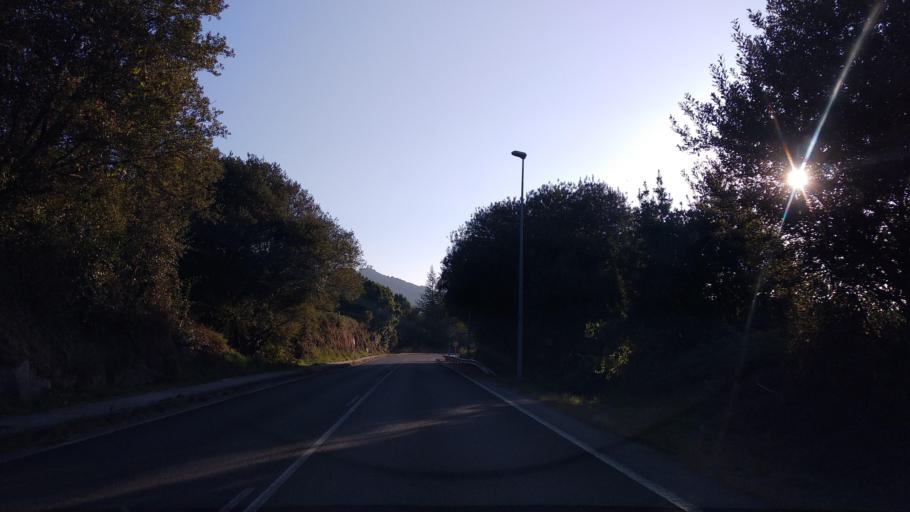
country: ES
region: Galicia
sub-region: Provincia de Pontevedra
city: Redondela
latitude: 42.3397
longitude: -8.5655
